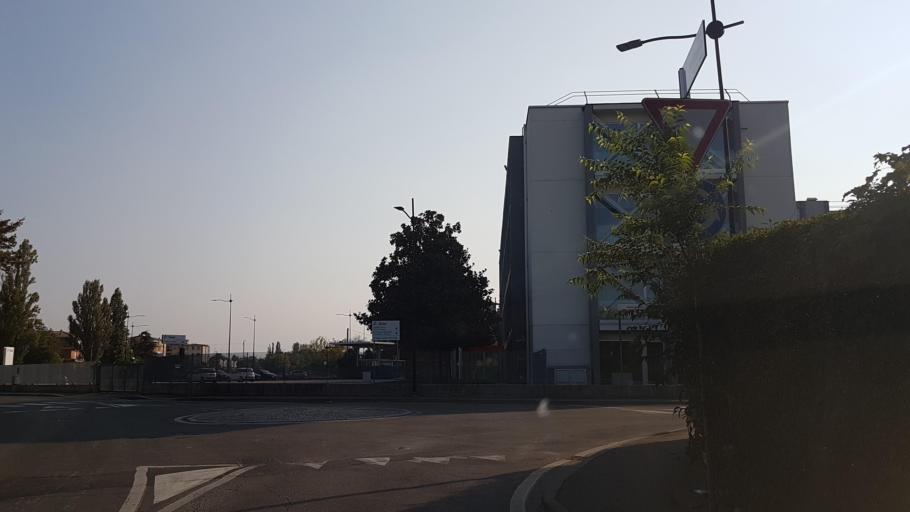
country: IT
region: Emilia-Romagna
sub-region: Provincia di Parma
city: Vicofertile
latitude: 44.7806
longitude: 10.2825
